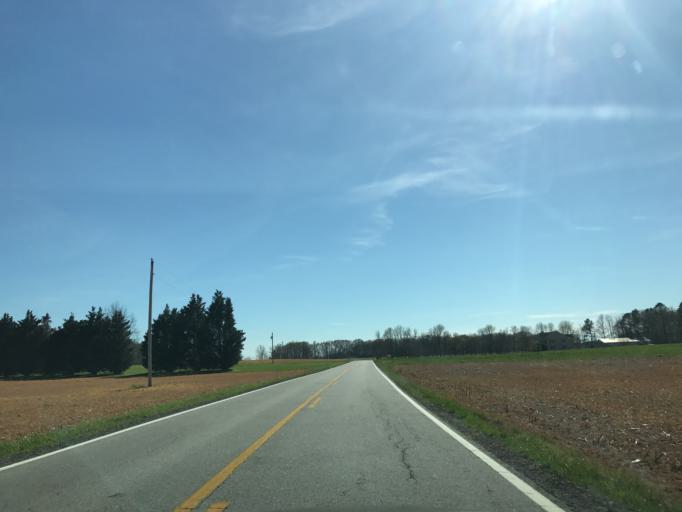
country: US
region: Maryland
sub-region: Caroline County
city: Ridgely
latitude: 38.9684
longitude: -75.9749
